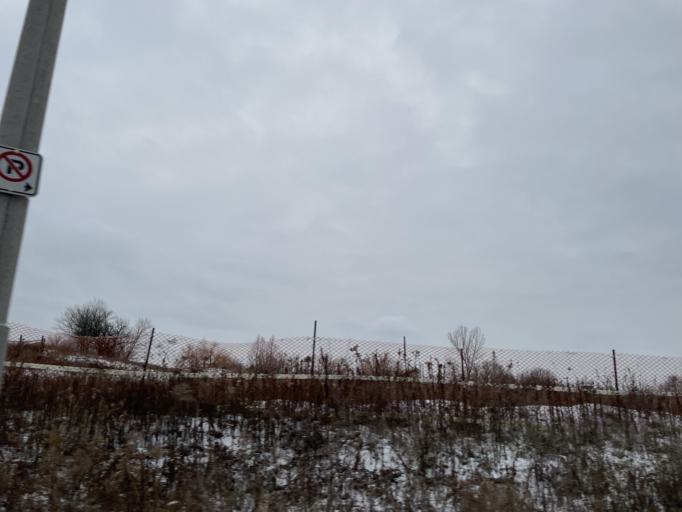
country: CA
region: Ontario
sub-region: Wellington County
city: Guelph
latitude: 43.4974
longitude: -80.1890
